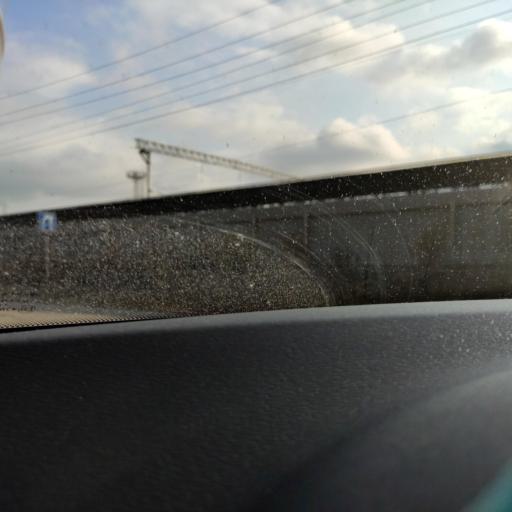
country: RU
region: Samara
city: Samara
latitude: 53.1862
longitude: 50.1247
